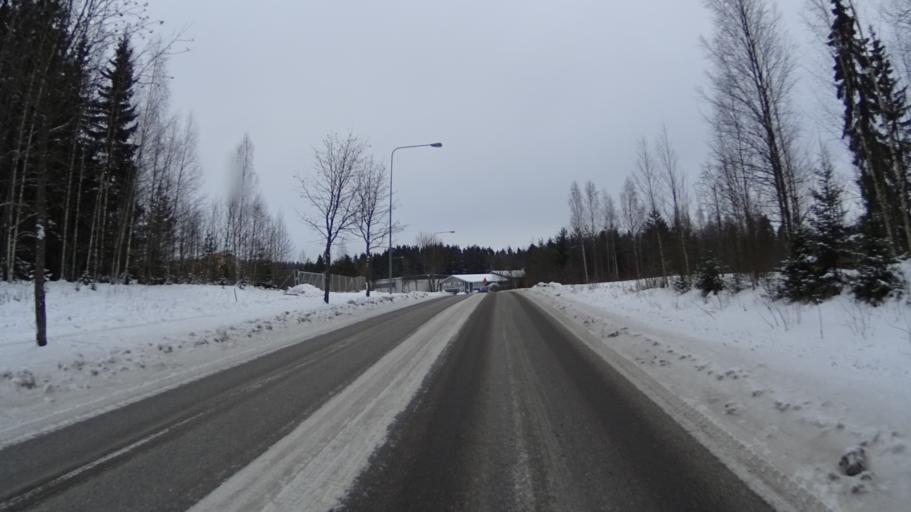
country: FI
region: Uusimaa
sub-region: Helsinki
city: Karkkila
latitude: 60.5308
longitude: 24.2347
